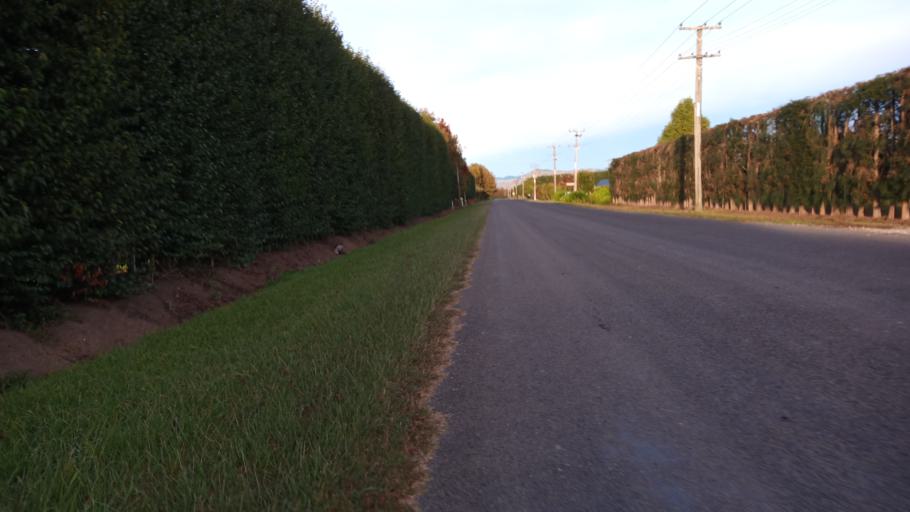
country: NZ
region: Gisborne
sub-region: Gisborne District
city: Gisborne
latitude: -38.6524
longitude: 177.9404
